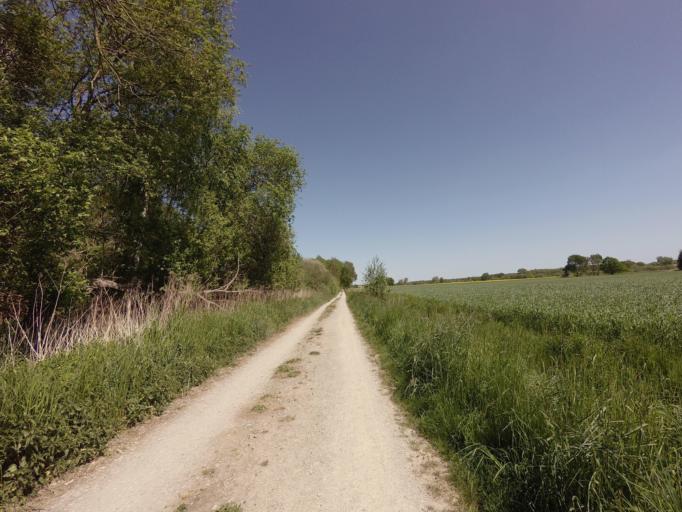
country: DE
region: Lower Saxony
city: Braunschweig
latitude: 52.3047
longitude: 10.5846
